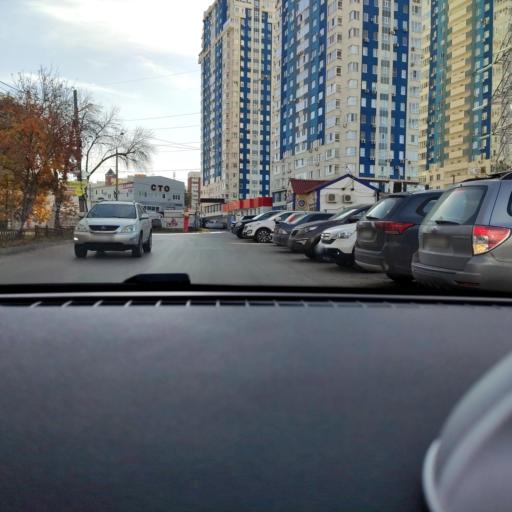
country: RU
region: Samara
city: Samara
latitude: 53.2233
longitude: 50.1528
